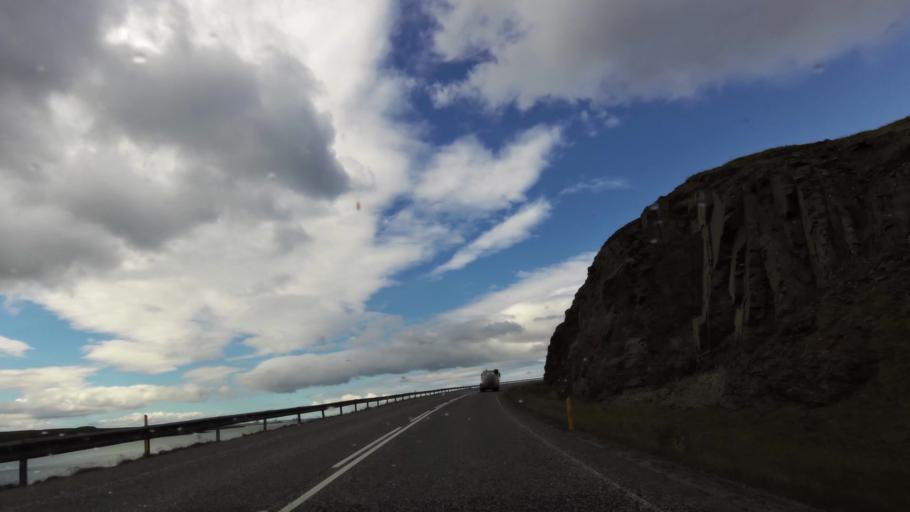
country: IS
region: Capital Region
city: Mosfellsbaer
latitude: 64.2062
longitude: -21.7446
